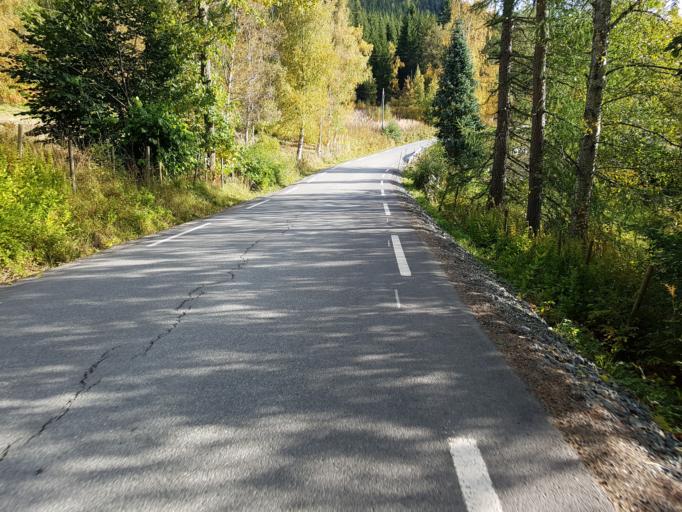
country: NO
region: Sor-Trondelag
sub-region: Malvik
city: Malvik
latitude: 63.3573
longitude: 10.6381
